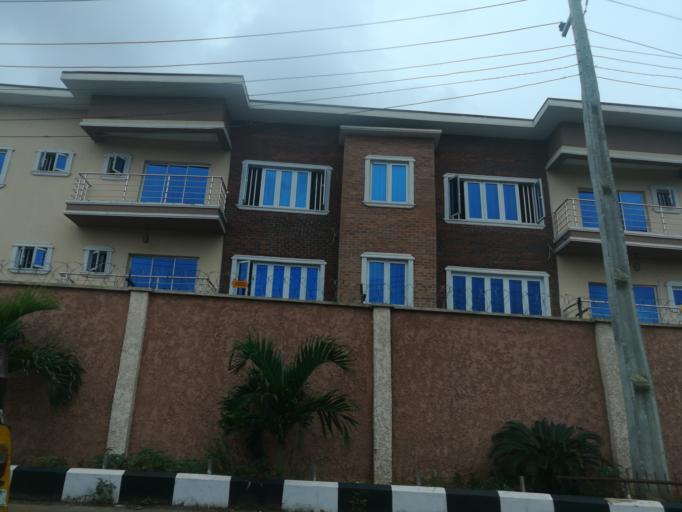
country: NG
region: Lagos
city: Agege
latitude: 6.6210
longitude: 3.3460
